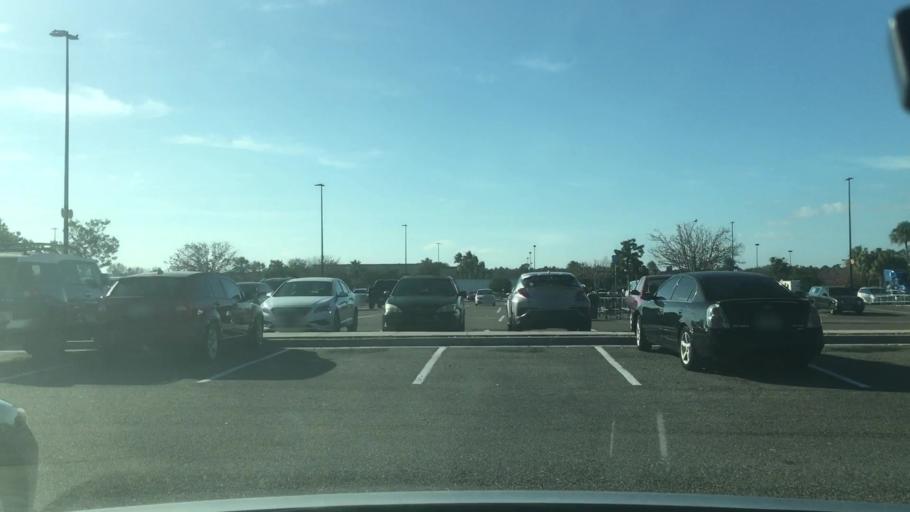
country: US
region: Florida
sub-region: Duval County
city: Atlantic Beach
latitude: 30.3186
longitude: -81.4912
